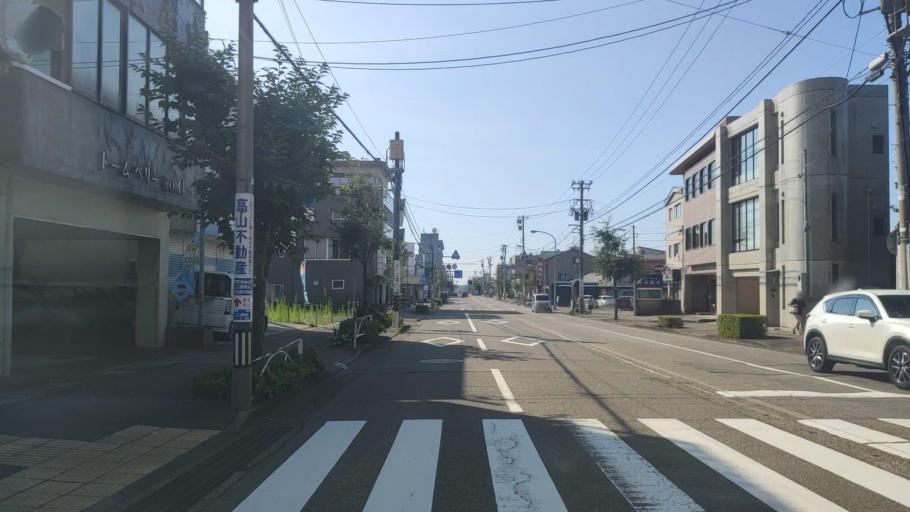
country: JP
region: Ishikawa
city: Nonoichi
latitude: 36.5438
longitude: 136.6785
